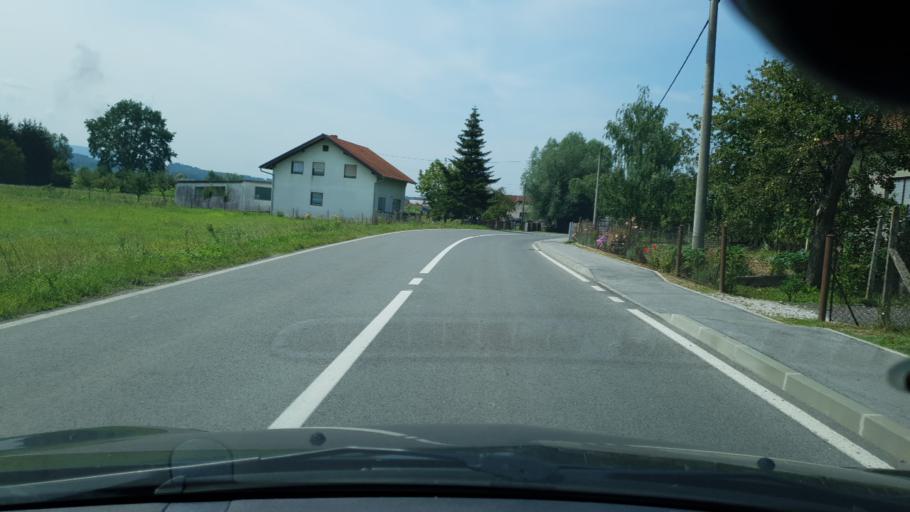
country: HR
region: Krapinsko-Zagorska
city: Bedekovcina
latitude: 46.0304
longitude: 15.9667
